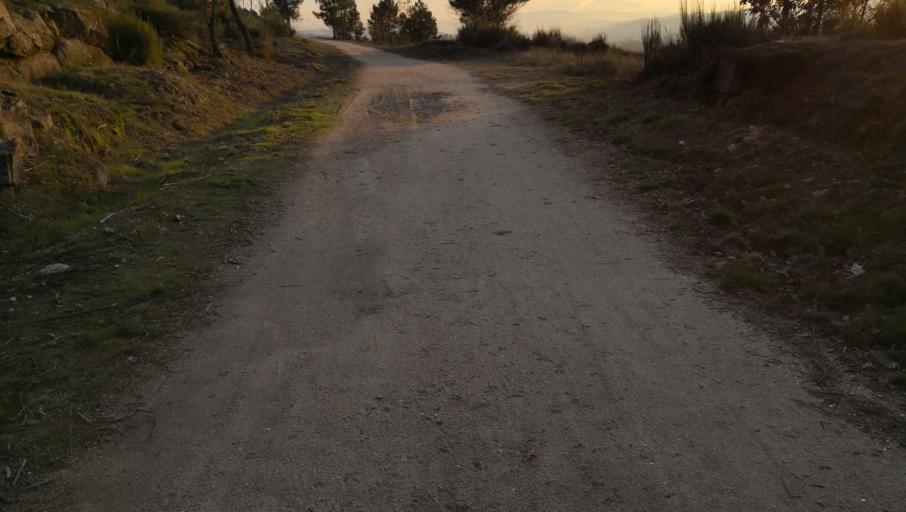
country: PT
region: Vila Real
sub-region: Vila Real
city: Vila Real
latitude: 41.3374
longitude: -7.7094
